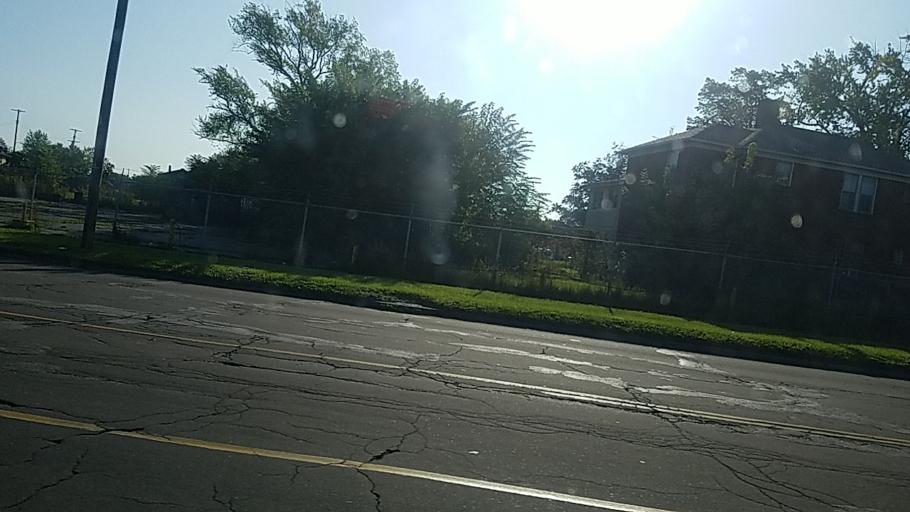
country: US
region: Ohio
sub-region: Mahoning County
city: Youngstown
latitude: 41.0668
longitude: -80.6613
